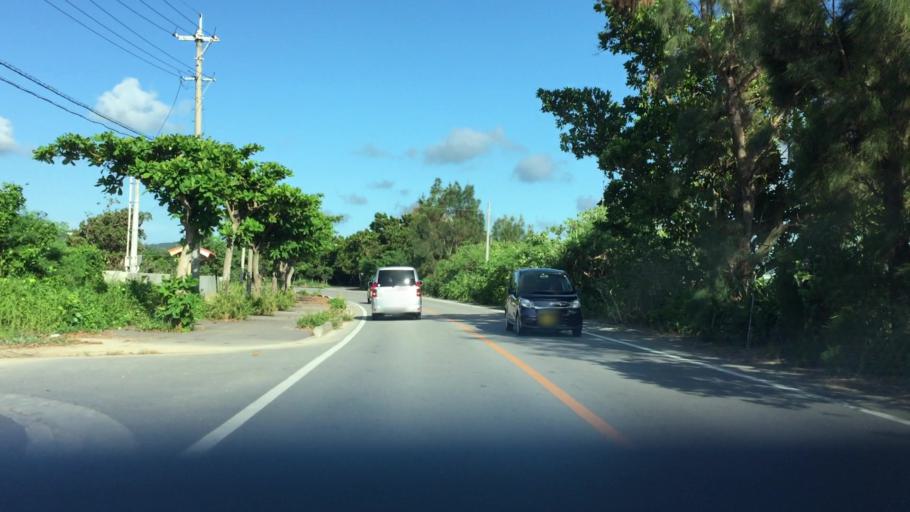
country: JP
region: Okinawa
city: Ishigaki
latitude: 24.4152
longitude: 124.1354
